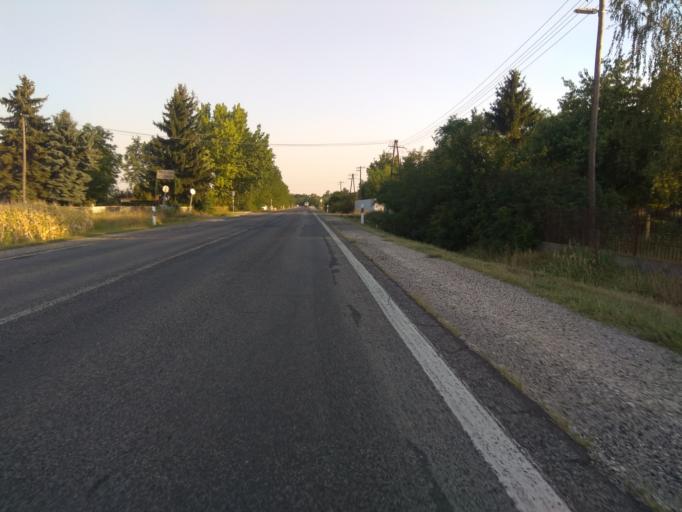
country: HU
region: Borsod-Abauj-Zemplen
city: Nyekladhaza
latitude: 47.9740
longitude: 20.8302
